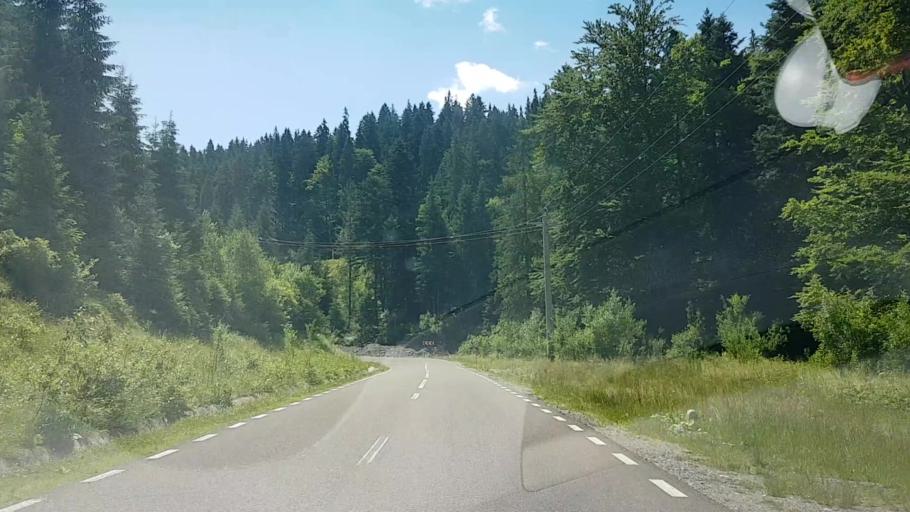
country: RO
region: Suceava
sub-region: Comuna Sadova
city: Sadova
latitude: 47.4650
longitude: 25.5155
